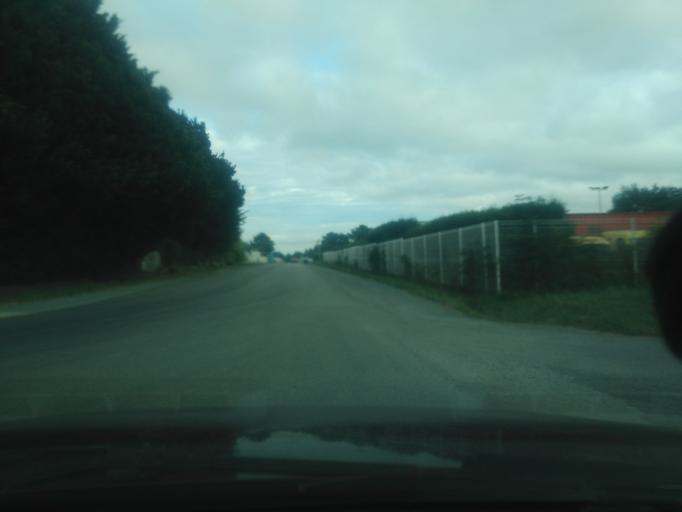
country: FR
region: Pays de la Loire
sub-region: Departement de la Vendee
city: Dompierre-sur-Yon
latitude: 46.6943
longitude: -1.3726
